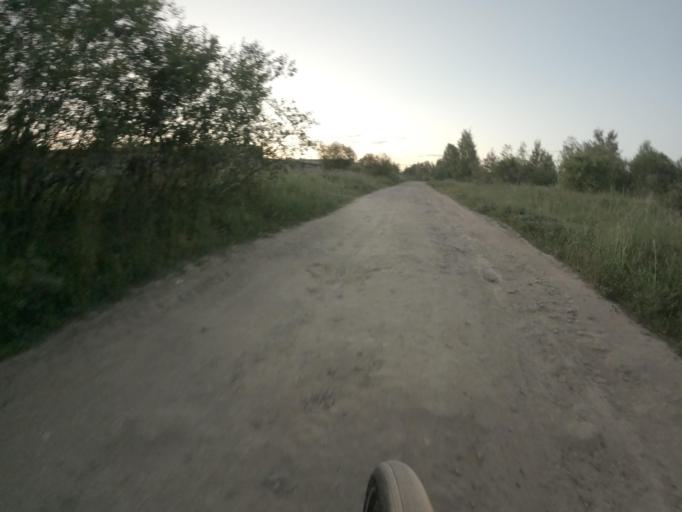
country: RU
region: St.-Petersburg
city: Sapernyy
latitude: 59.7818
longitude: 30.6736
